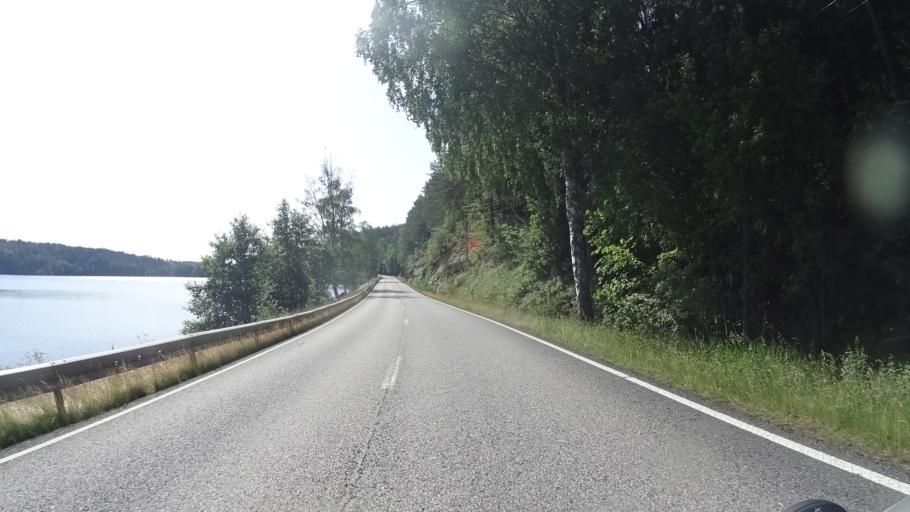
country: SE
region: Kalmar
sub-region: Vasterviks Kommun
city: Overum
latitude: 58.0031
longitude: 16.2752
